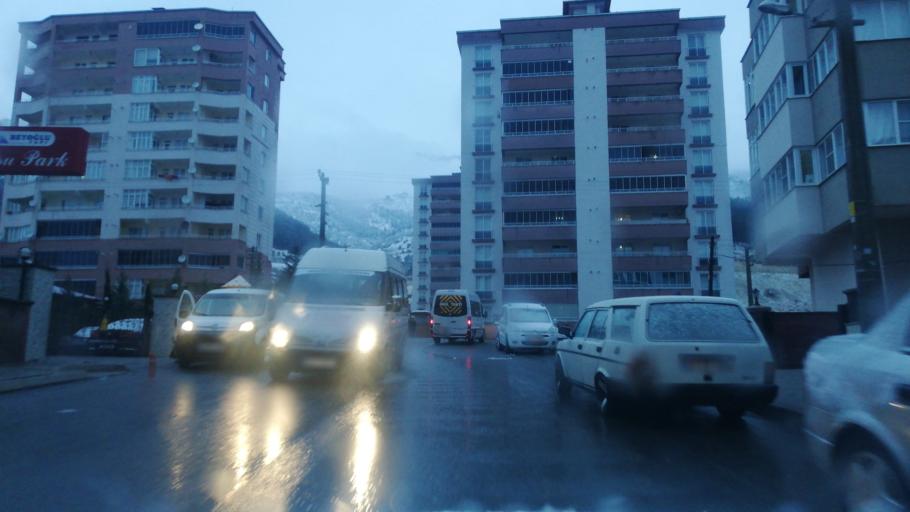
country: TR
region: Kahramanmaras
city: Kahramanmaras
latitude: 37.6001
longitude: 36.8823
